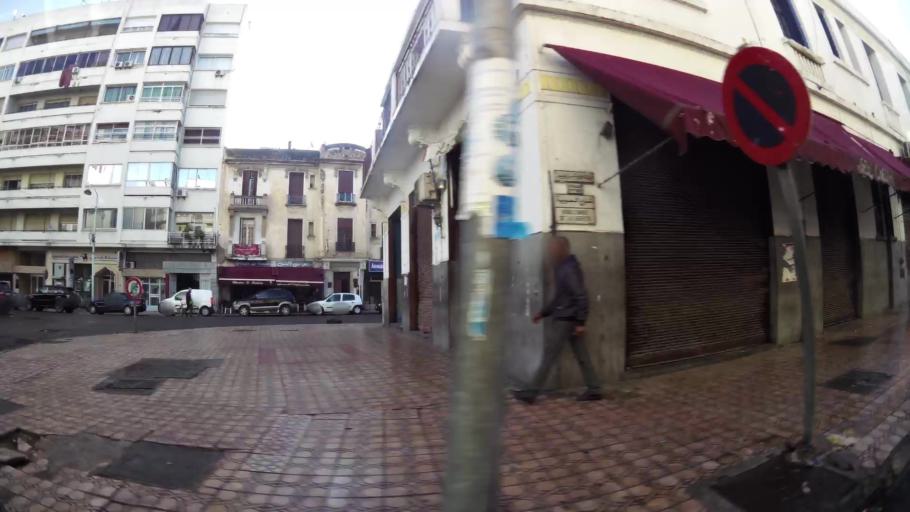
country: MA
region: Grand Casablanca
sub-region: Casablanca
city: Casablanca
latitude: 33.5873
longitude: -7.6119
